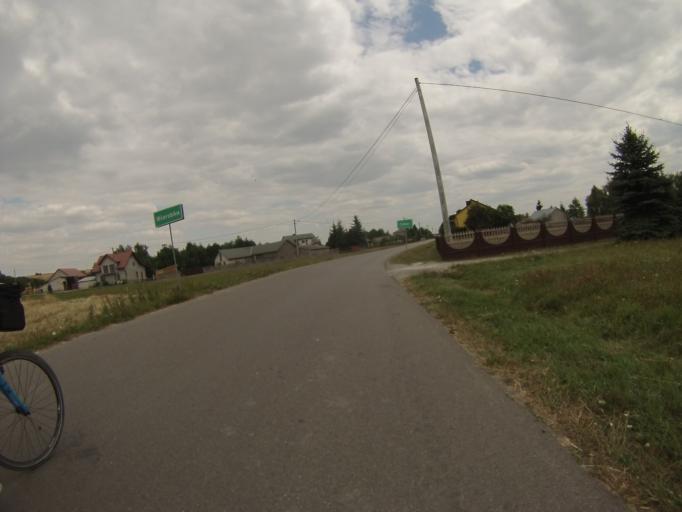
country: PL
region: Swietokrzyskie
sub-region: Powiat staszowski
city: Bogoria
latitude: 50.6866
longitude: 21.2118
